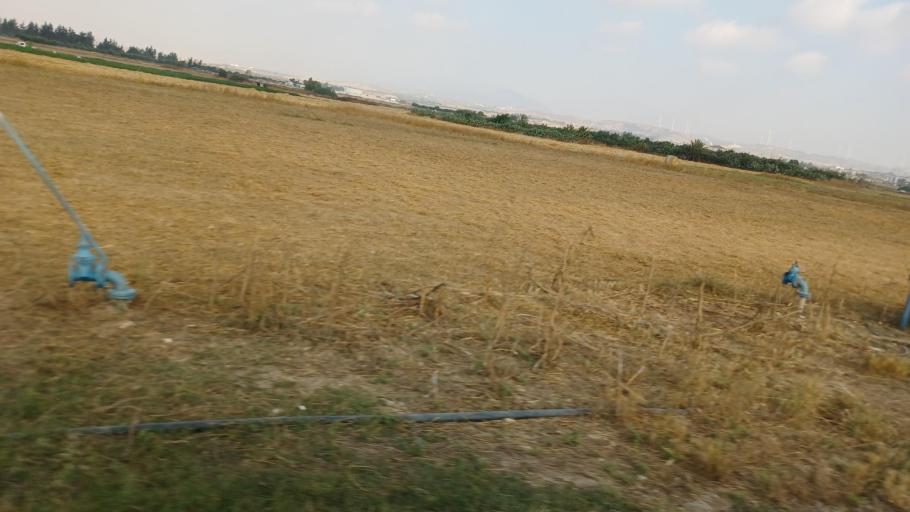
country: CY
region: Larnaka
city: Kiti
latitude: 34.8318
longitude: 33.5557
